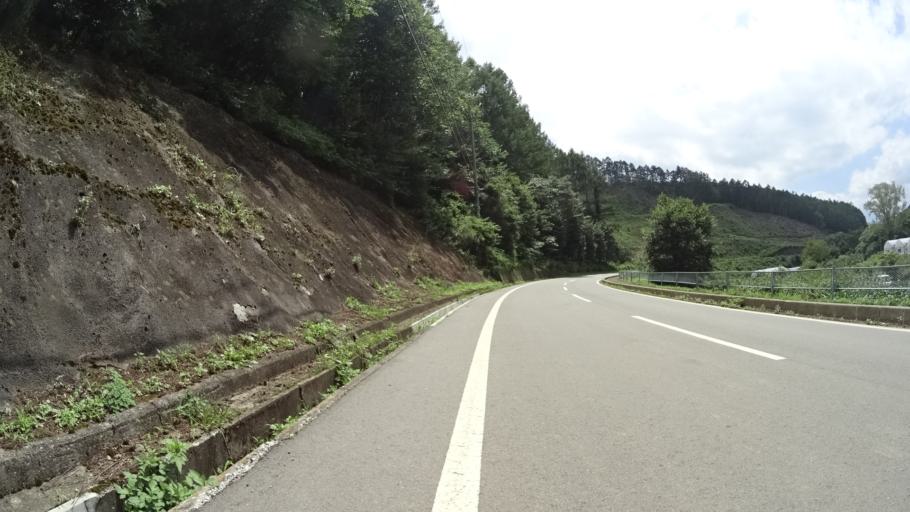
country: JP
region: Nagano
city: Saku
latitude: 36.0617
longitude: 138.5847
